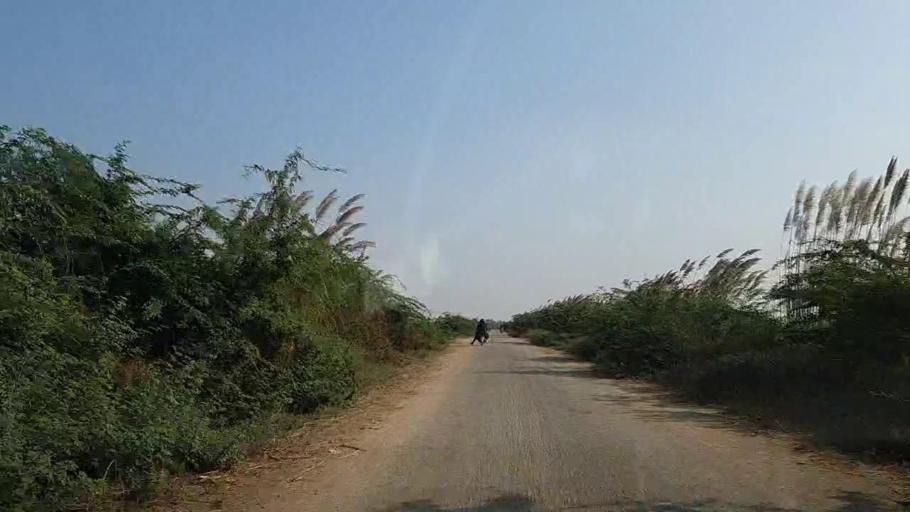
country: PK
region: Sindh
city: Mirpur Sakro
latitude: 24.6240
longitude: 67.6561
